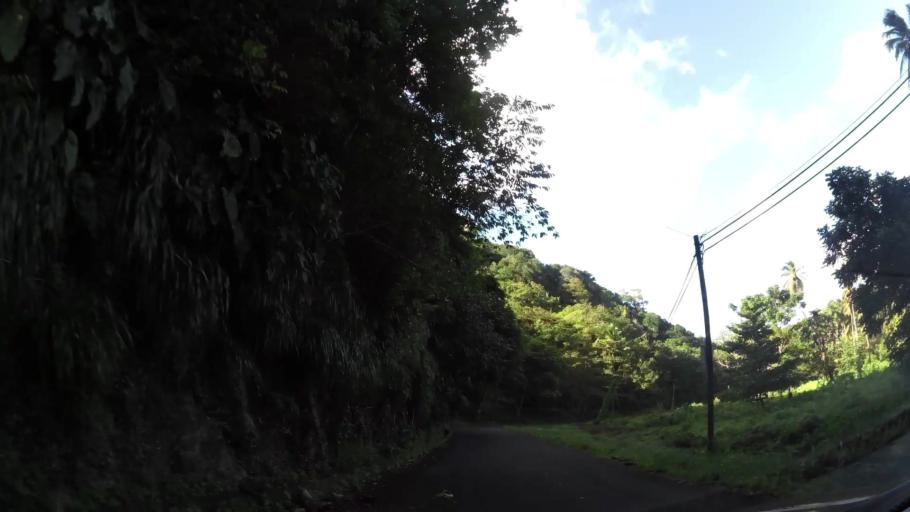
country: DM
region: Saint Andrew
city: Calibishie
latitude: 15.5912
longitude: -61.3910
